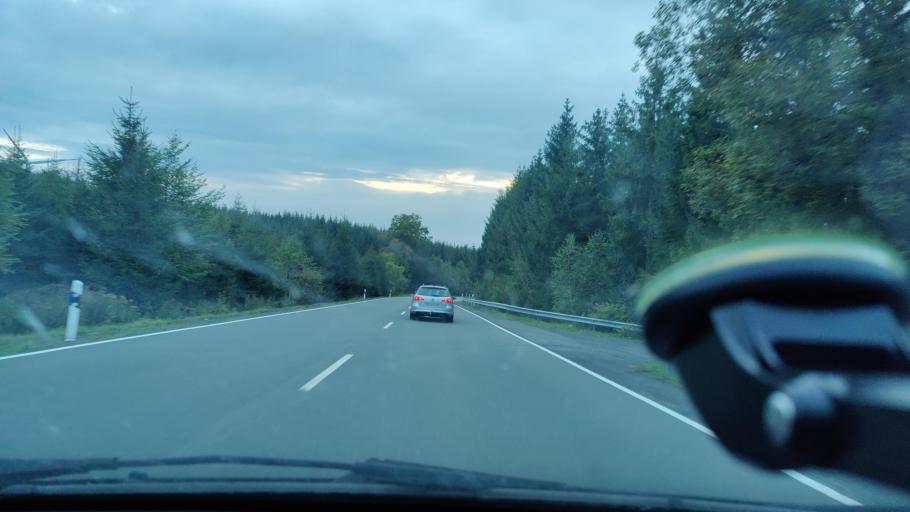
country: DE
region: North Rhine-Westphalia
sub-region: Regierungsbezirk Arnsberg
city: Wilnsdorf
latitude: 50.7991
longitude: 8.1263
